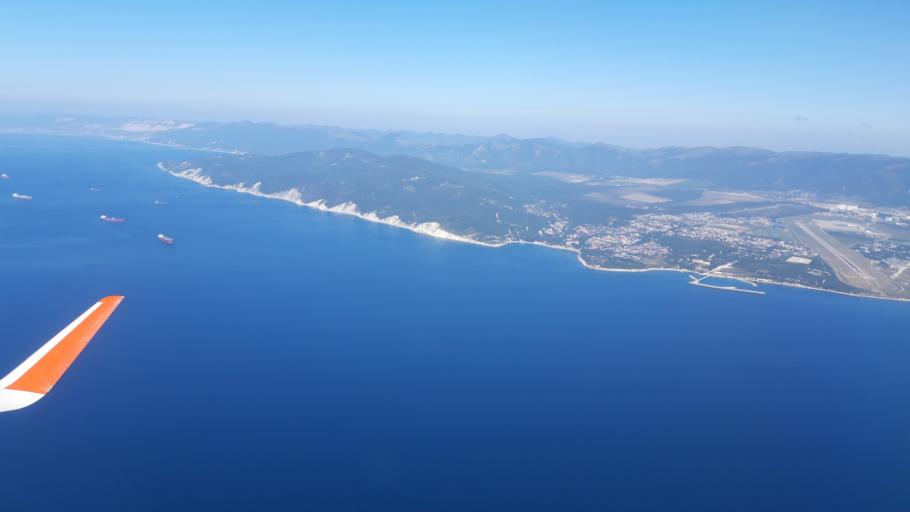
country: RU
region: Krasnodarskiy
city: Gelendzhik
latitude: 44.5241
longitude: 37.9751
